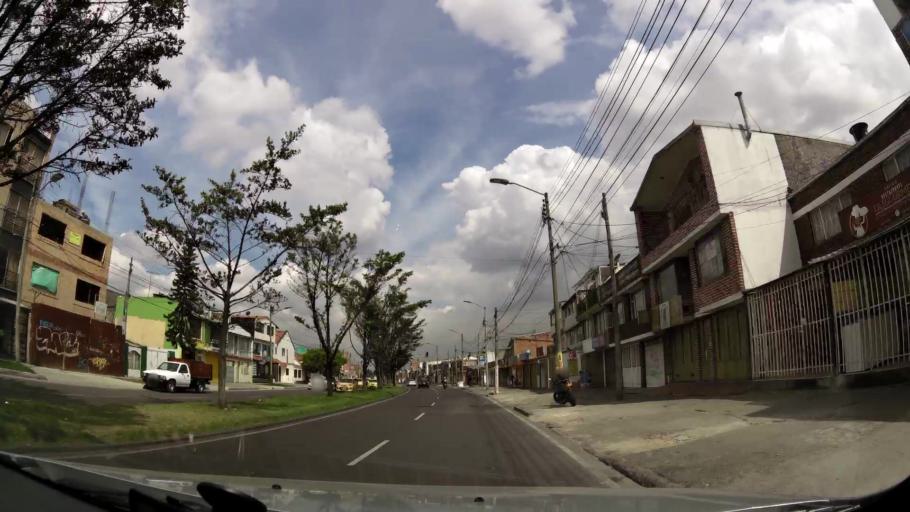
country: CO
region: Bogota D.C.
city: Bogota
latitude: 4.6056
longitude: -74.1147
